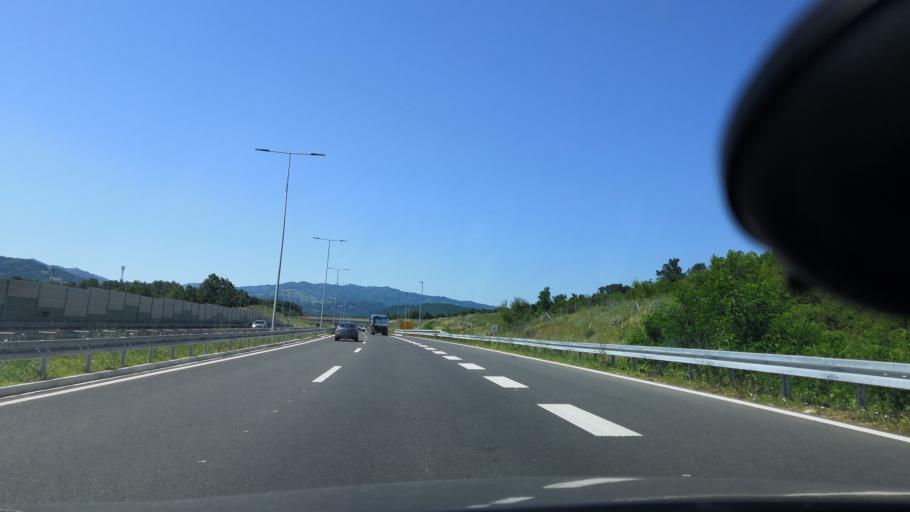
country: RS
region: Central Serbia
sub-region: Pcinjski Okrug
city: Vladicin Han
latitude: 42.7004
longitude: 22.0758
